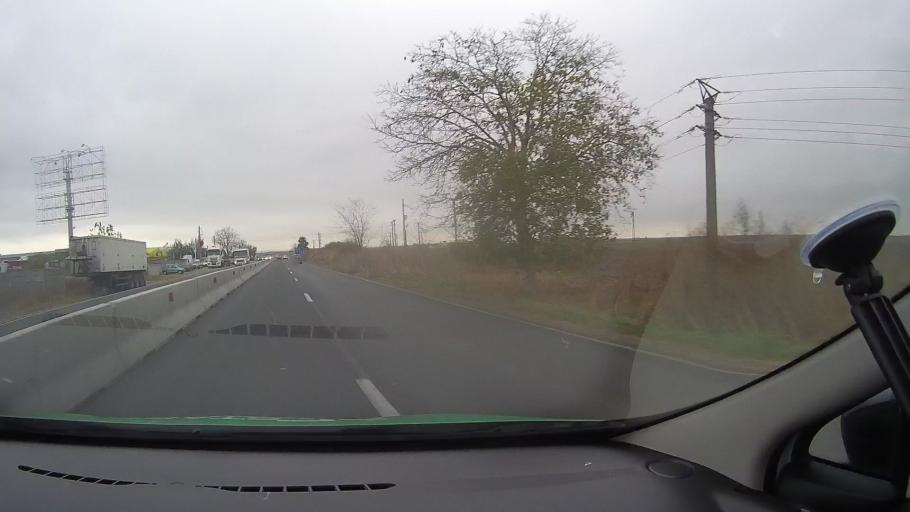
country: RO
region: Constanta
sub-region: Comuna Cumpana
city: Cumpana
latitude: 44.1675
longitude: 28.5586
